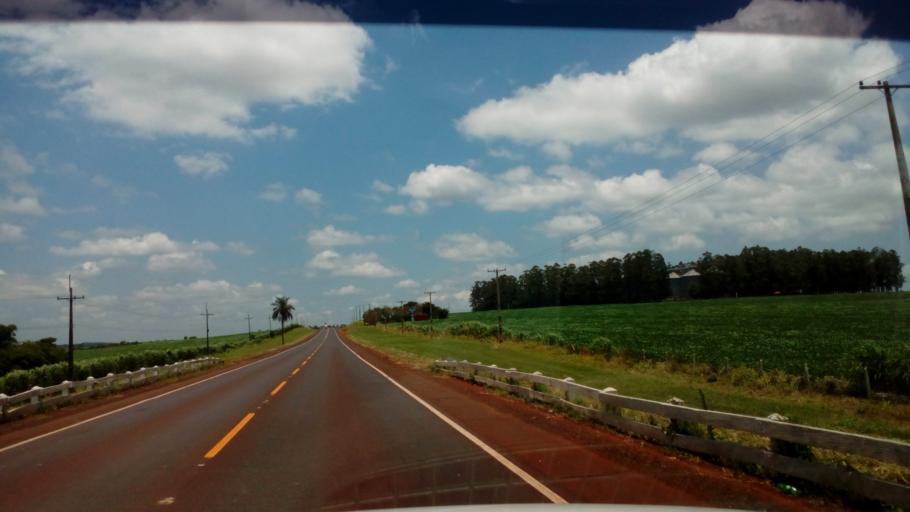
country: PY
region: Alto Parana
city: Naranjal
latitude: -26.0556
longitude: -55.1362
